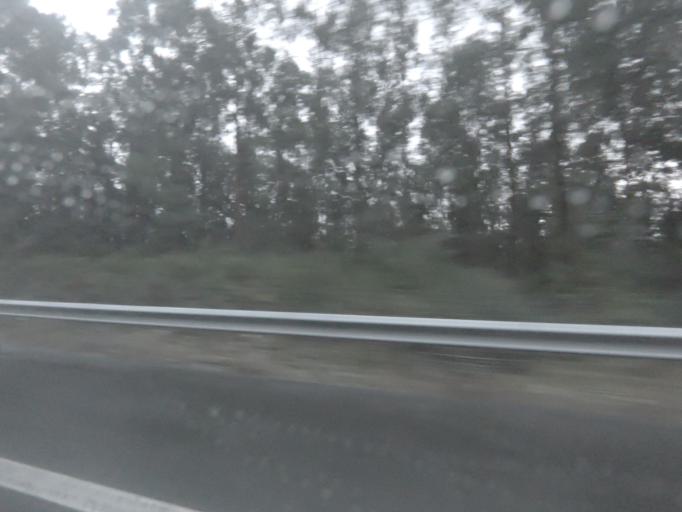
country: ES
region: Galicia
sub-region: Provincia de Pontevedra
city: Marin
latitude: 42.3416
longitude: -8.6481
